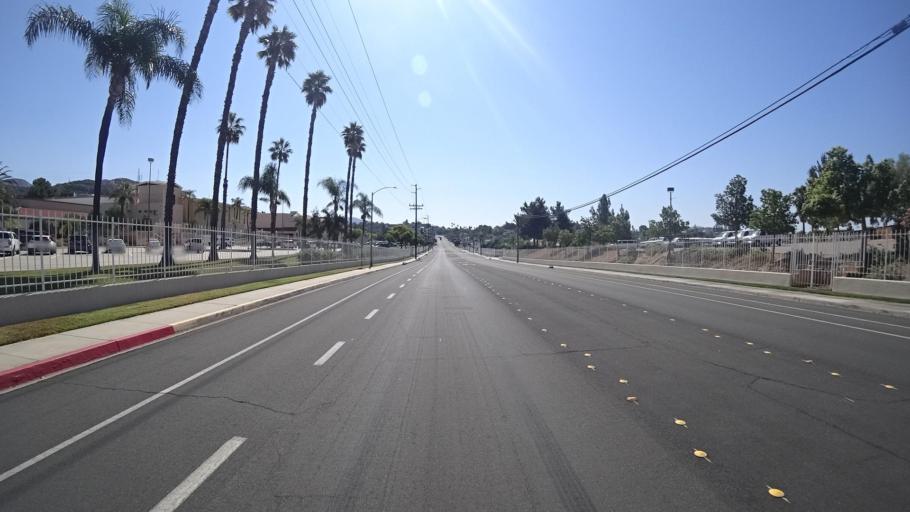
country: US
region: California
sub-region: San Diego County
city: Granite Hills
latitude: 32.8000
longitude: -116.9042
